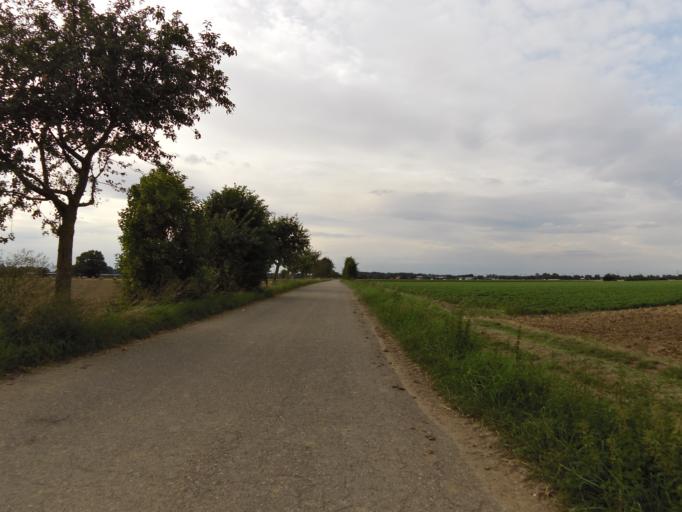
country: DE
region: Rheinland-Pfalz
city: Worms
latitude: 49.6212
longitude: 8.4075
